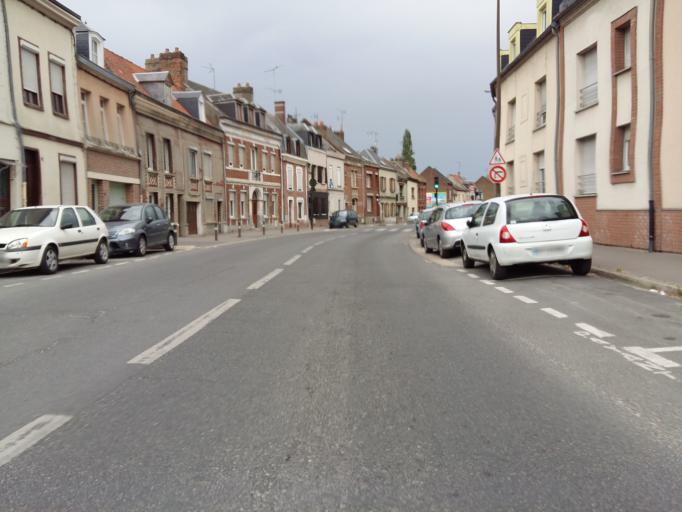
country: FR
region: Picardie
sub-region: Departement de la Somme
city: Rivery
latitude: 49.8940
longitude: 2.3126
